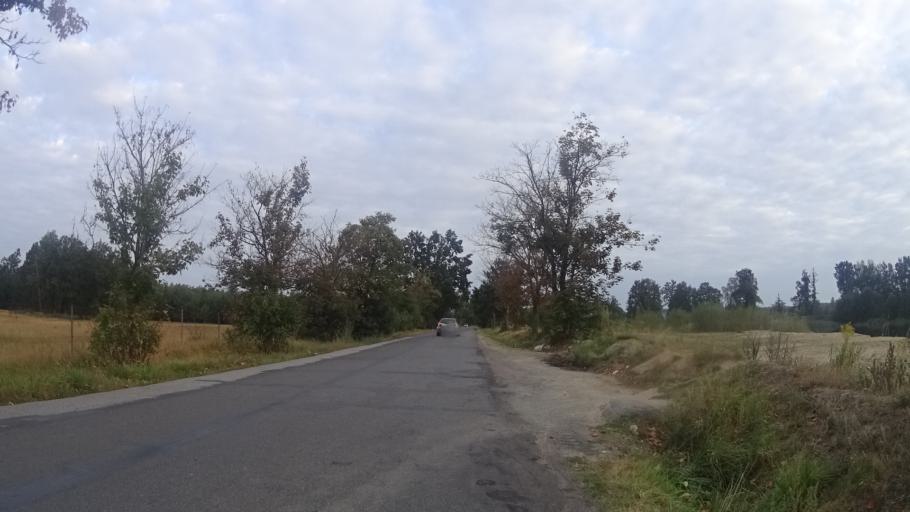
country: CZ
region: Kralovehradecky
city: Trebechovice pod Orebem
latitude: 50.2013
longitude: 15.9314
